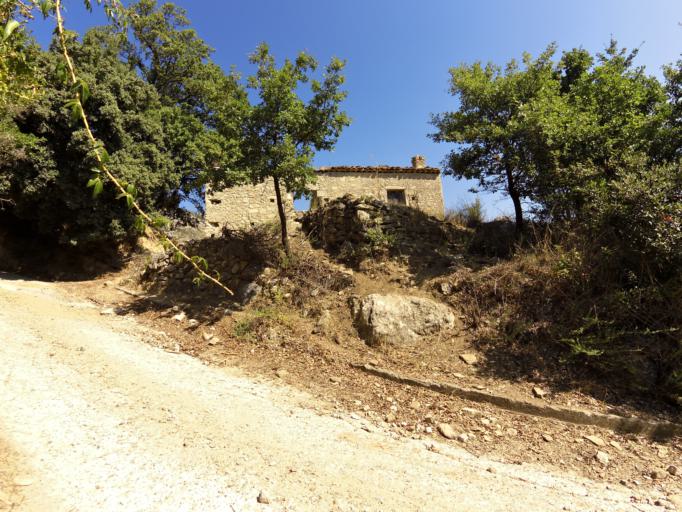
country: IT
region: Calabria
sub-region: Provincia di Reggio Calabria
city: Pazzano
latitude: 38.4542
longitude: 16.4436
